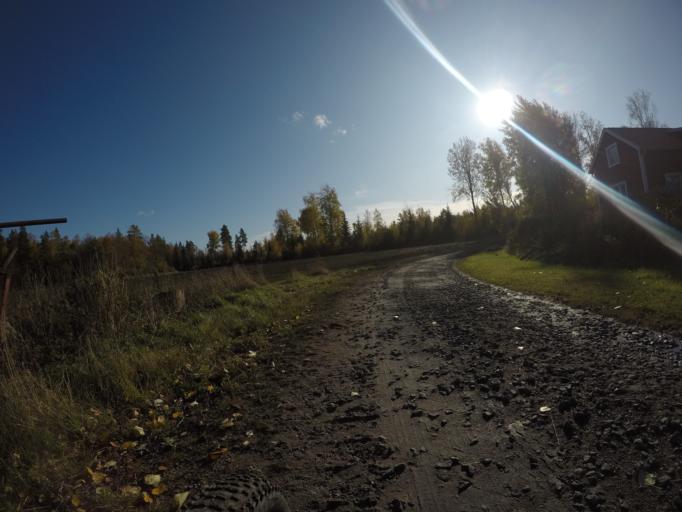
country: SE
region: Vaestmanland
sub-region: Kungsors Kommun
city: Kungsoer
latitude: 59.3157
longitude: 16.0987
